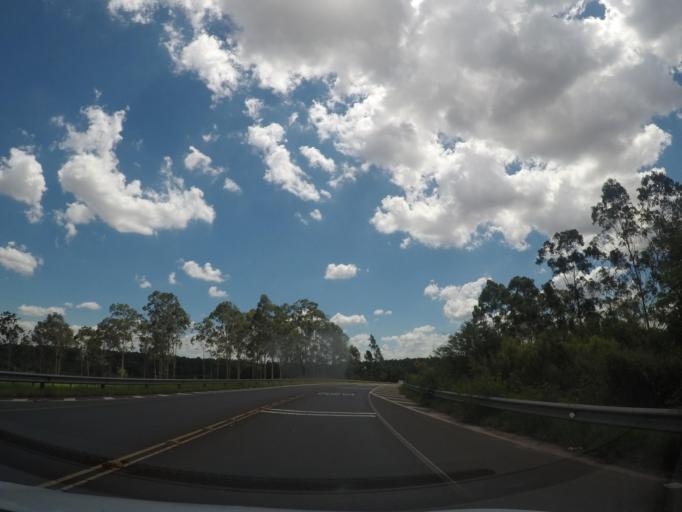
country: BR
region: Sao Paulo
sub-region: Sumare
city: Sumare
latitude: -22.8465
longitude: -47.2503
